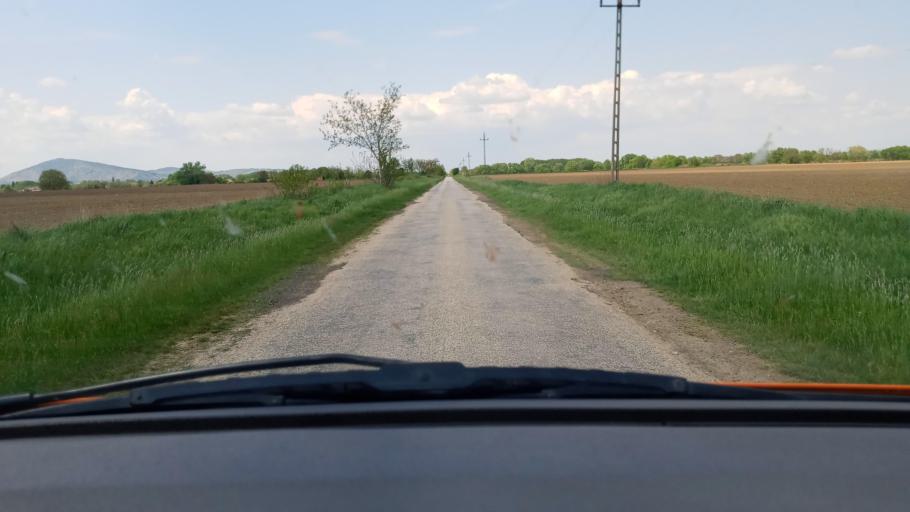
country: HU
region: Baranya
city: Villany
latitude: 45.8114
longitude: 18.5140
